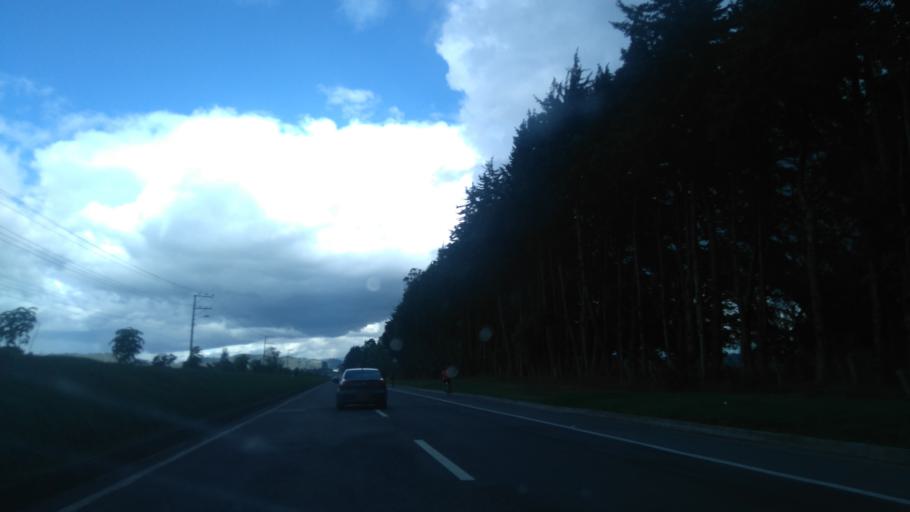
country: CO
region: Cundinamarca
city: El Rosal
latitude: 4.8460
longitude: -74.2670
